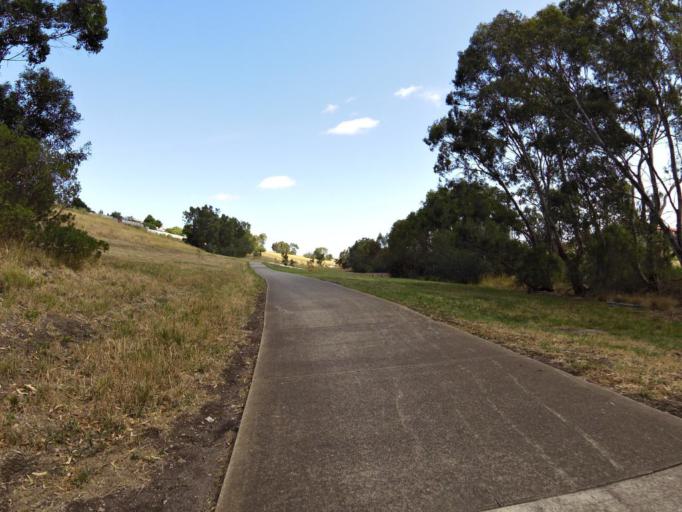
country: AU
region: Victoria
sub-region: Hume
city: Meadow Heights
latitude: -37.6539
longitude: 144.9092
